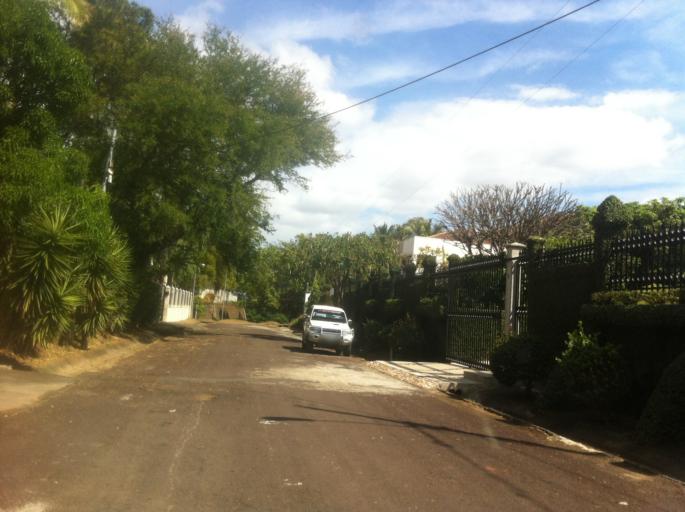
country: NI
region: Managua
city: El Crucero
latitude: 12.0737
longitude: -86.3217
